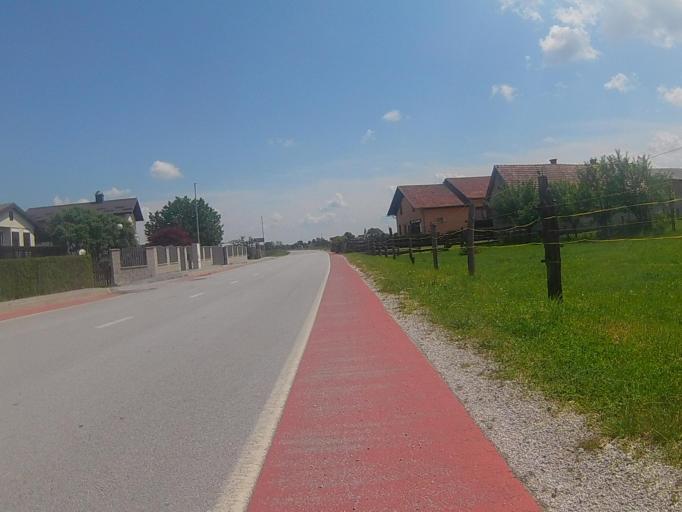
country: SI
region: Starse
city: Starse
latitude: 46.4488
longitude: 15.7496
